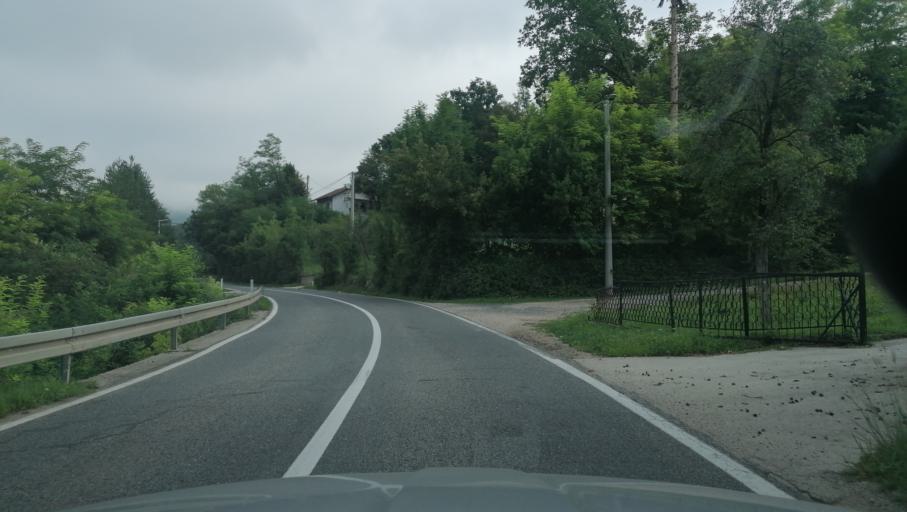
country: BA
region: Federation of Bosnia and Herzegovina
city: Divicani
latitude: 44.3582
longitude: 17.3001
